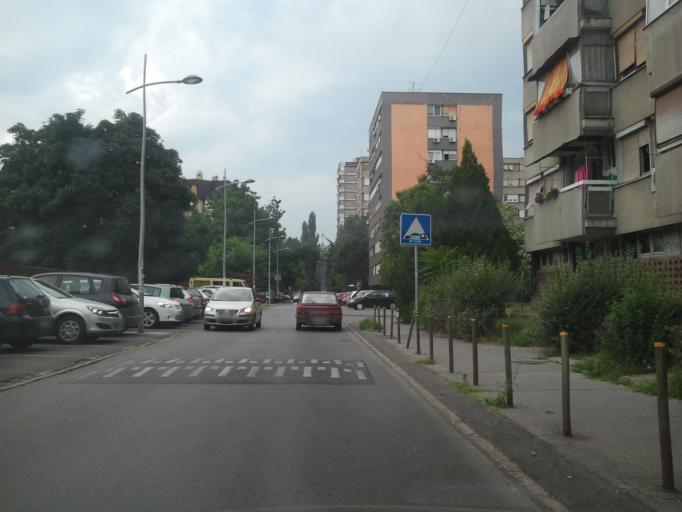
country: RS
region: Autonomna Pokrajina Vojvodina
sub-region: Juznobacki Okrug
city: Novi Sad
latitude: 45.2415
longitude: 19.8450
